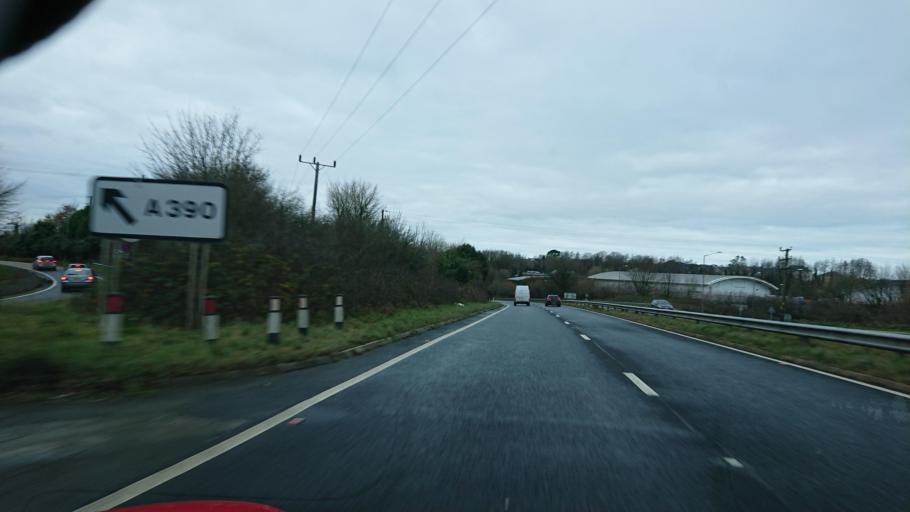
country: GB
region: England
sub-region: Cornwall
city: Liskeard
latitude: 50.4477
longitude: -4.4496
